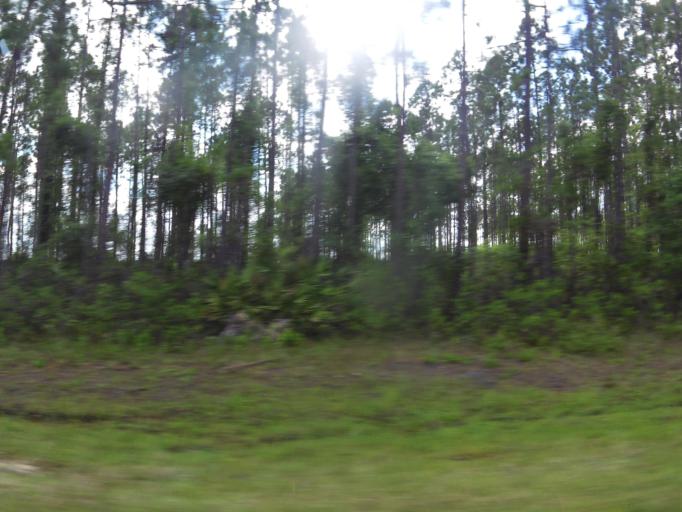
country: US
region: Florida
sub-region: Clay County
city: Green Cove Springs
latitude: 29.9664
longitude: -81.7393
